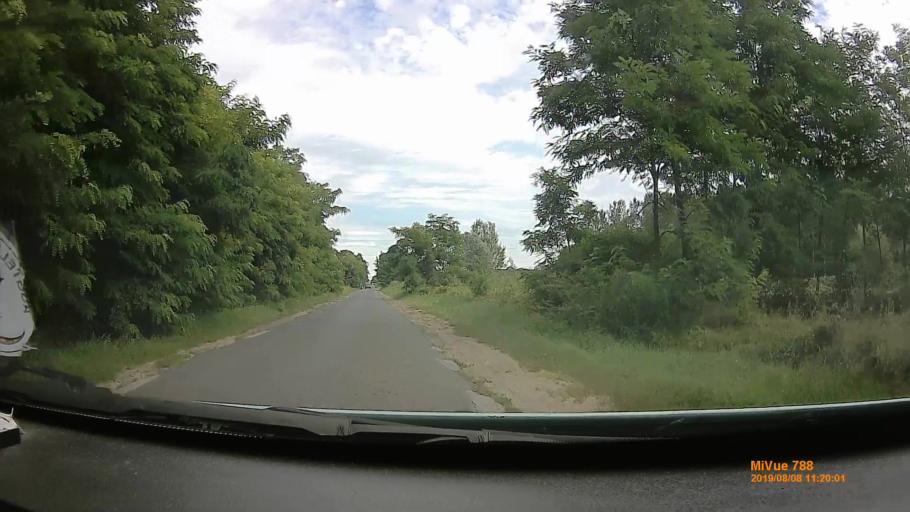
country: HU
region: Szabolcs-Szatmar-Bereg
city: Balkany
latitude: 47.7492
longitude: 21.8425
